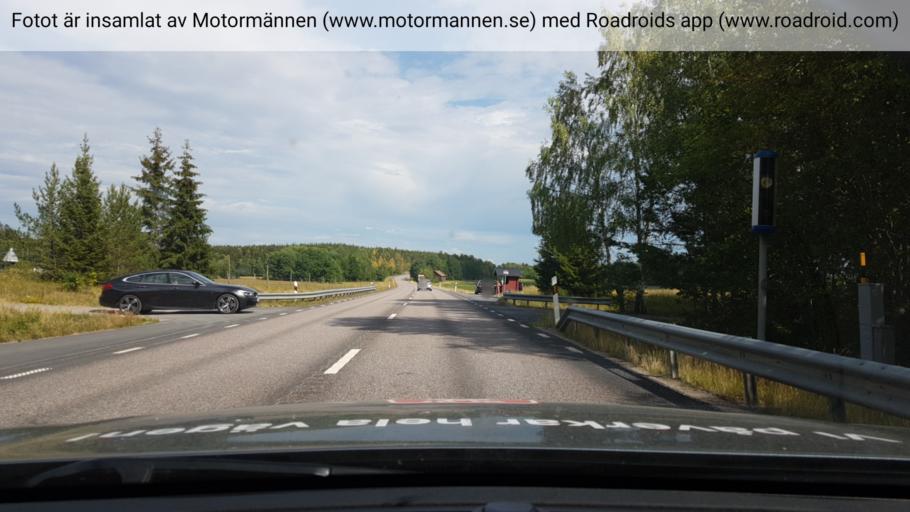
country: SE
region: Uppsala
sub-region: Enkopings Kommun
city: Orsundsbro
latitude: 59.8629
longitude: 17.3542
